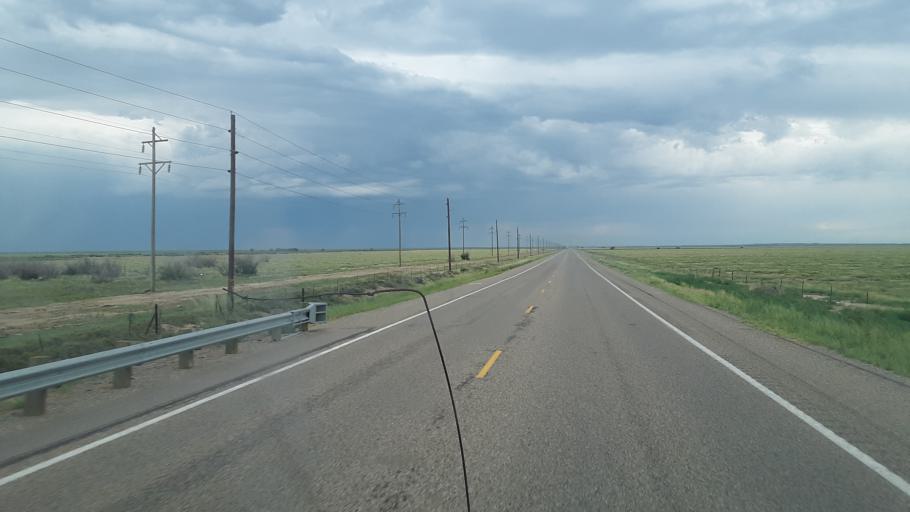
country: US
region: Colorado
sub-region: Crowley County
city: Ordway
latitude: 38.1819
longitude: -103.7482
